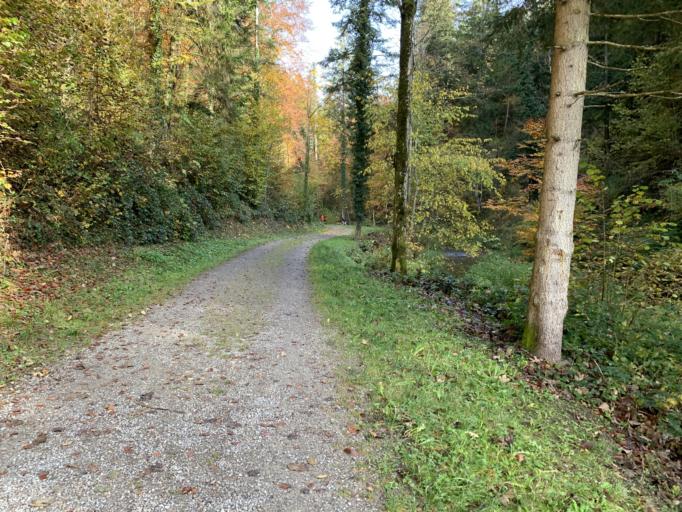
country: CH
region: Zurich
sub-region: Bezirk Hinwil
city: Hinwil
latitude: 47.3047
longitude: 8.8515
